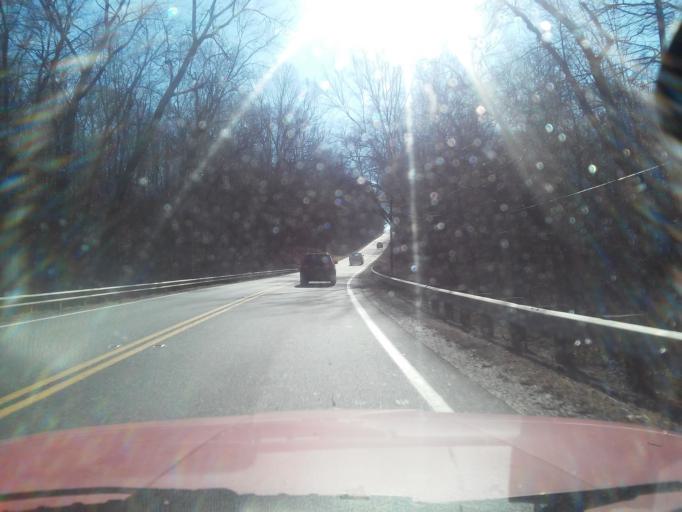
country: US
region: Virginia
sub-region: Orange County
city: Gordonsville
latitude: 38.0010
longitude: -78.1928
